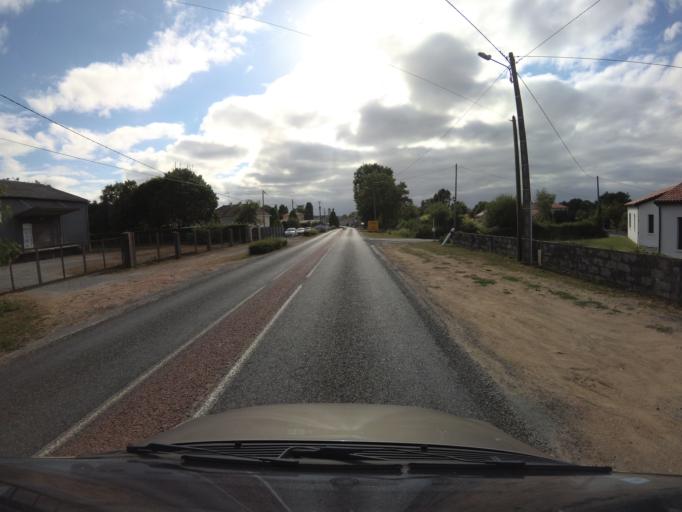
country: FR
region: Pays de la Loire
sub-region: Departement de Maine-et-Loire
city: Vezins
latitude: 47.1208
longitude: -0.7031
